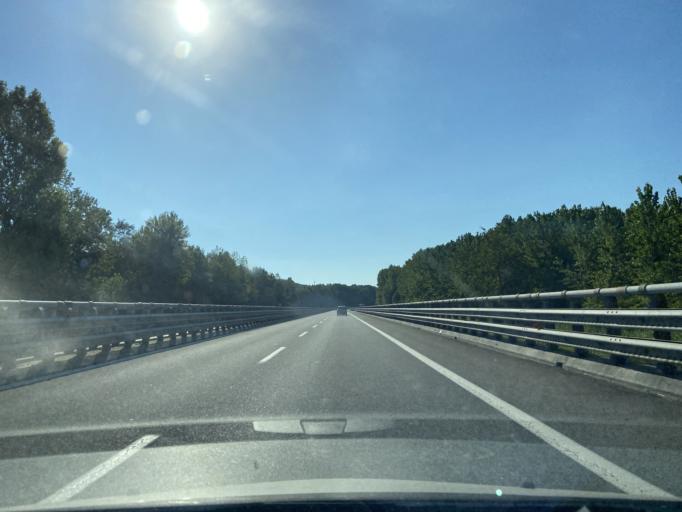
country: IT
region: Piedmont
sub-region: Provincia di Torino
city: Sant'Ambrogio di Torino
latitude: 45.1104
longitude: 7.3588
